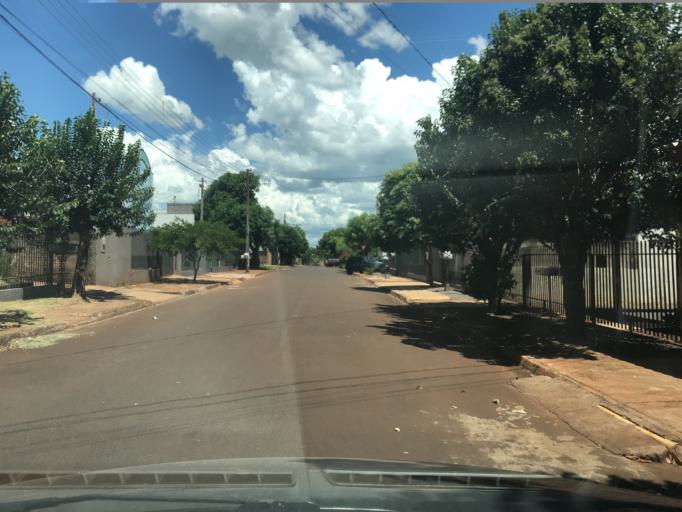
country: BR
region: Parana
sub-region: Palotina
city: Palotina
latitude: -24.2732
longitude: -53.8463
